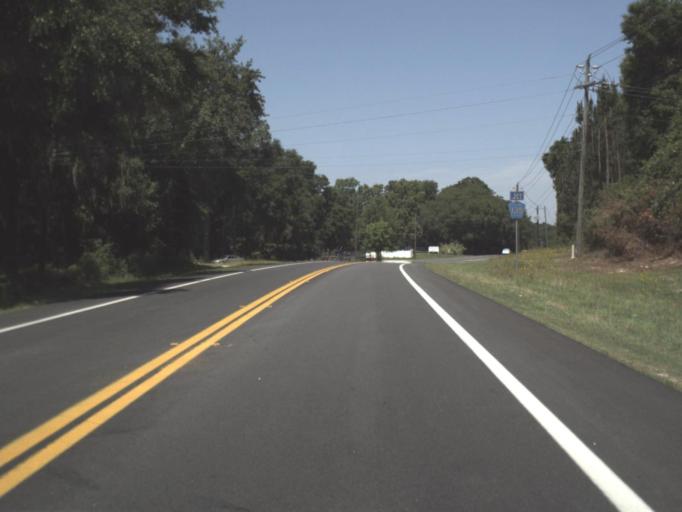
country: US
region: Florida
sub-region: Suwannee County
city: Wellborn
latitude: 30.1949
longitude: -82.7559
